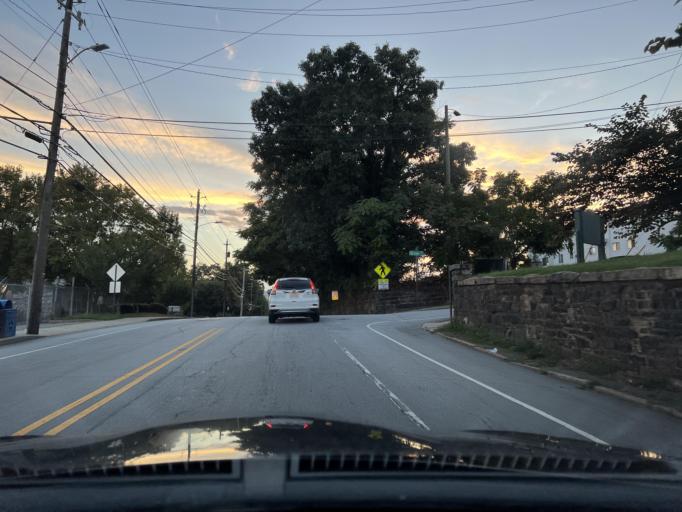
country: US
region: North Carolina
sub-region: Buncombe County
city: Asheville
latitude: 35.5912
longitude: -82.5574
